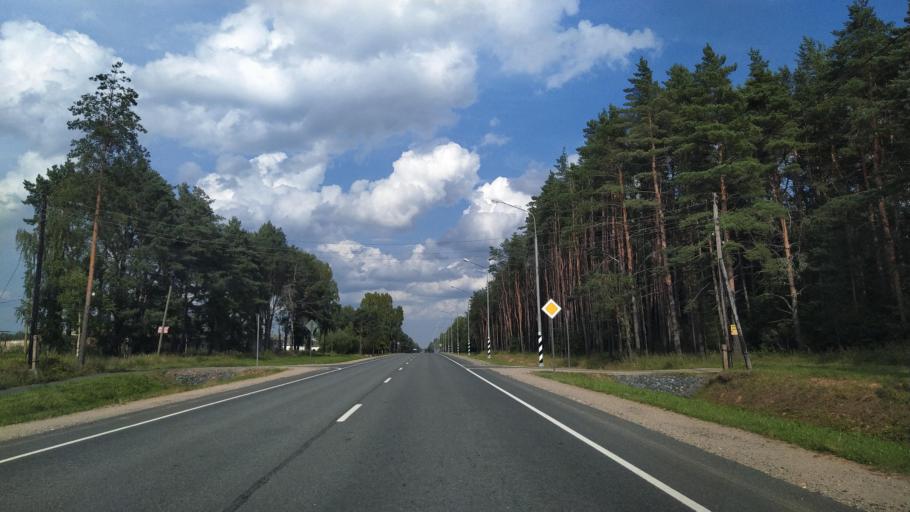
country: RU
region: Novgorod
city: Shimsk
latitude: 58.1790
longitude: 30.5341
